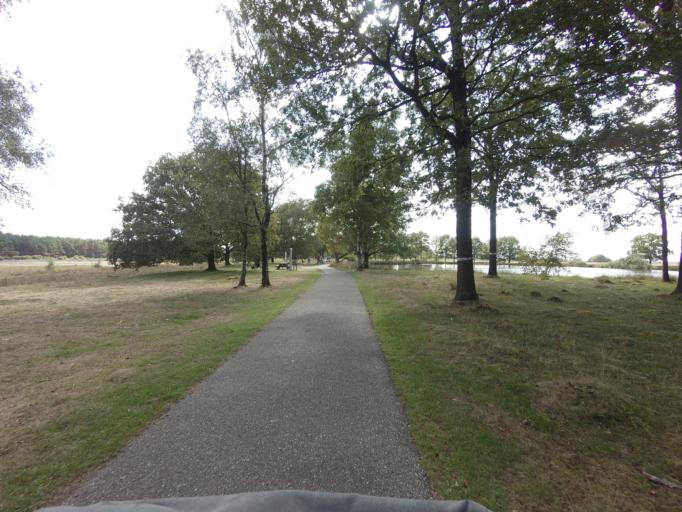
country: NL
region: Drenthe
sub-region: Gemeente Westerveld
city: Dwingeloo
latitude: 52.8020
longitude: 6.4469
